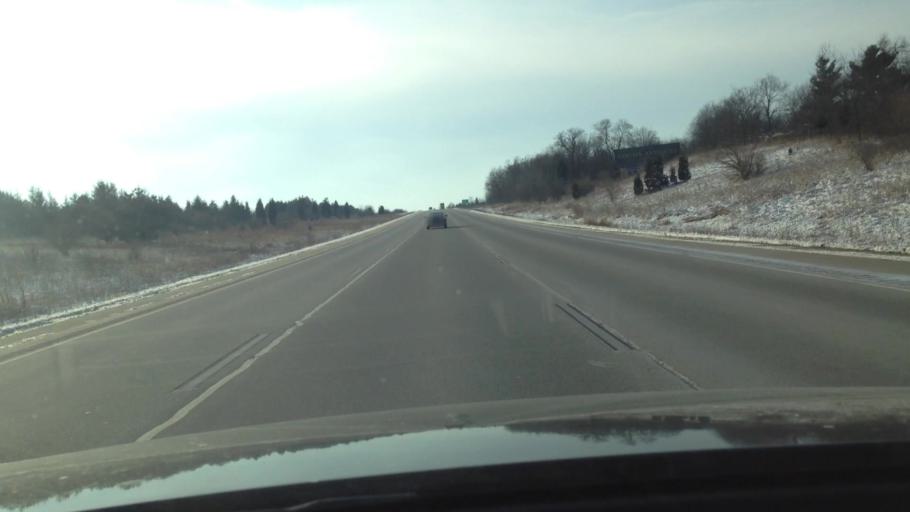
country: US
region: Wisconsin
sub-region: Walworth County
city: East Troy
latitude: 42.7709
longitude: -88.4166
